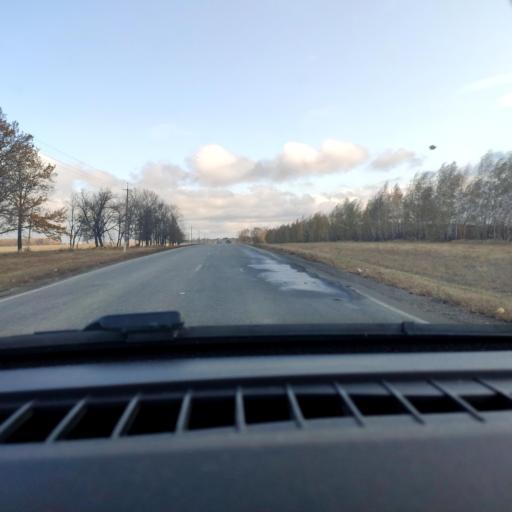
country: RU
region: Belgorod
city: Ilovka
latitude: 50.7146
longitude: 38.6670
